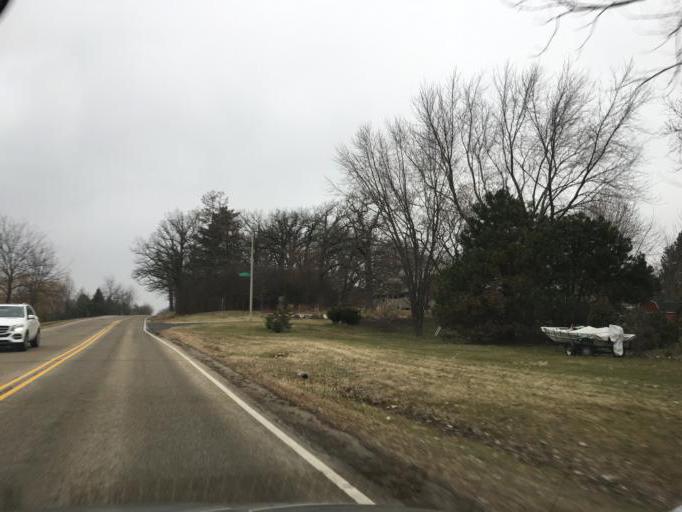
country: US
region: Illinois
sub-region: McHenry County
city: Lakewood
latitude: 42.2177
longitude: -88.3645
